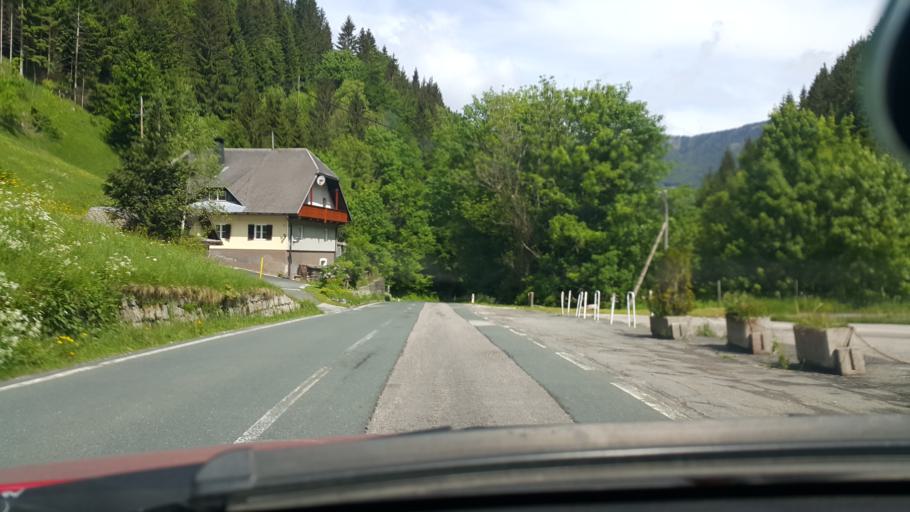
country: AT
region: Carinthia
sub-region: Politischer Bezirk Klagenfurt Land
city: Ferlach
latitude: 46.4610
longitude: 14.2585
